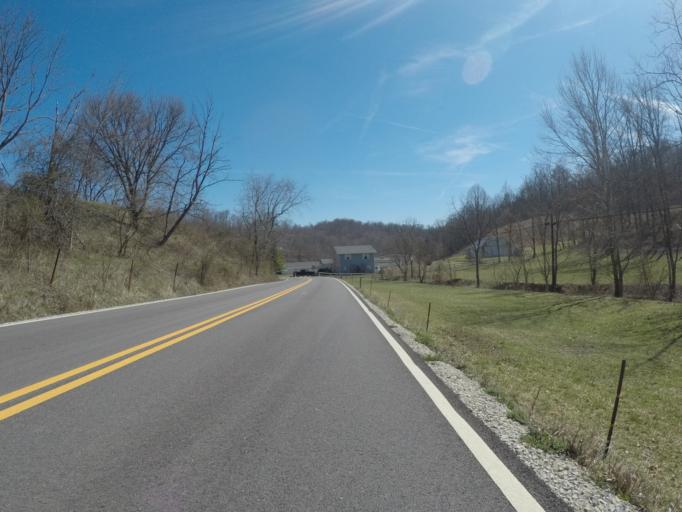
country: US
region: Ohio
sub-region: Lawrence County
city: Burlington
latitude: 38.4550
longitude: -82.5467
